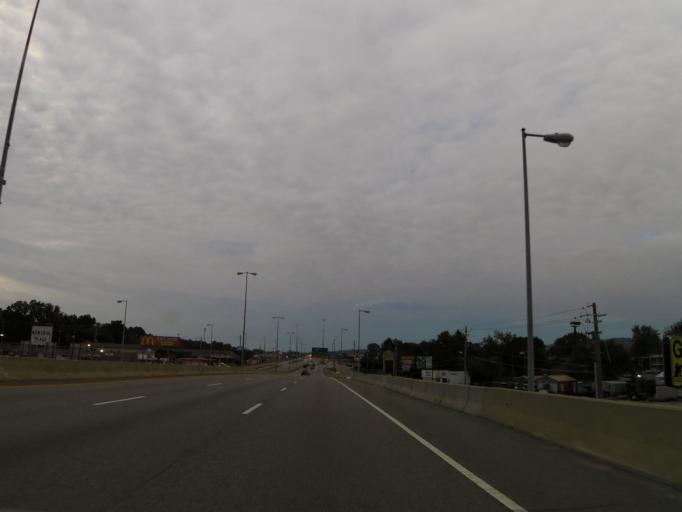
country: US
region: Alabama
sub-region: Madison County
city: Huntsville
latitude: 34.7497
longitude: -86.5986
